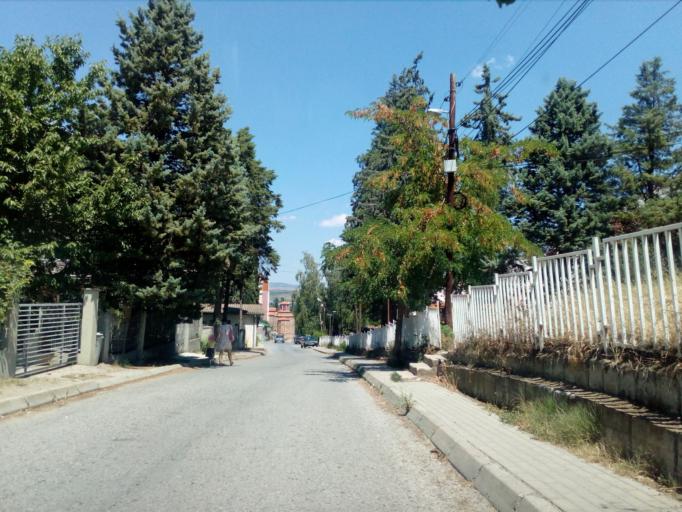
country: MK
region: Veles
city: Veles
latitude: 41.7154
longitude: 21.7744
